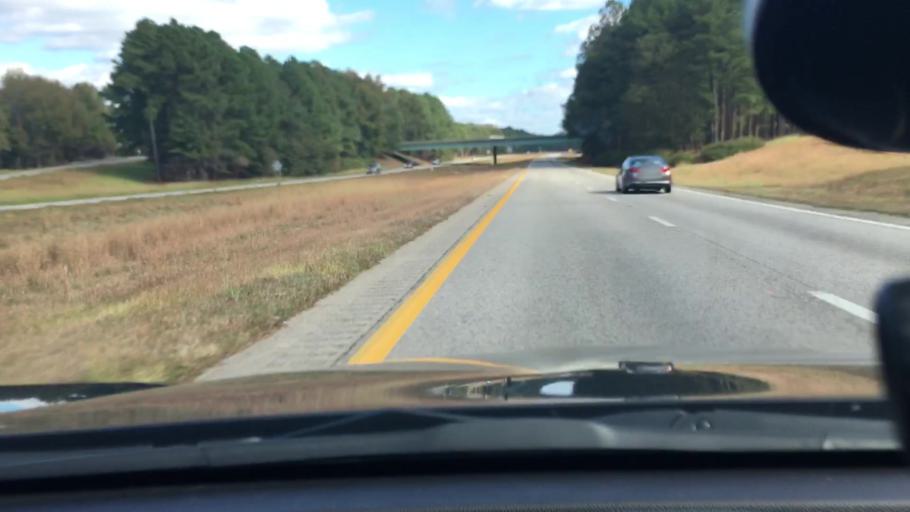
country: US
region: North Carolina
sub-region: Nash County
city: Spring Hope
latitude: 35.7876
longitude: -78.1200
